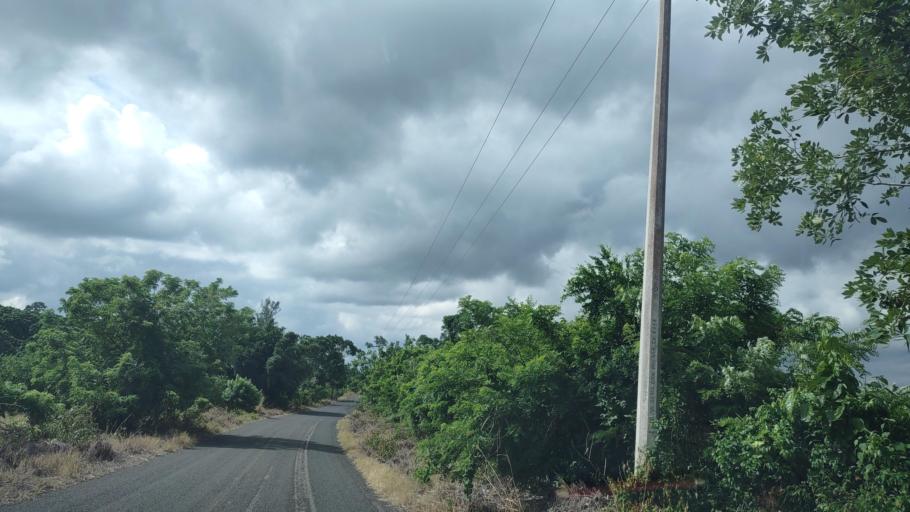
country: MX
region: Veracruz
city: Gutierrez Zamora
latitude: 20.2977
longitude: -97.1350
